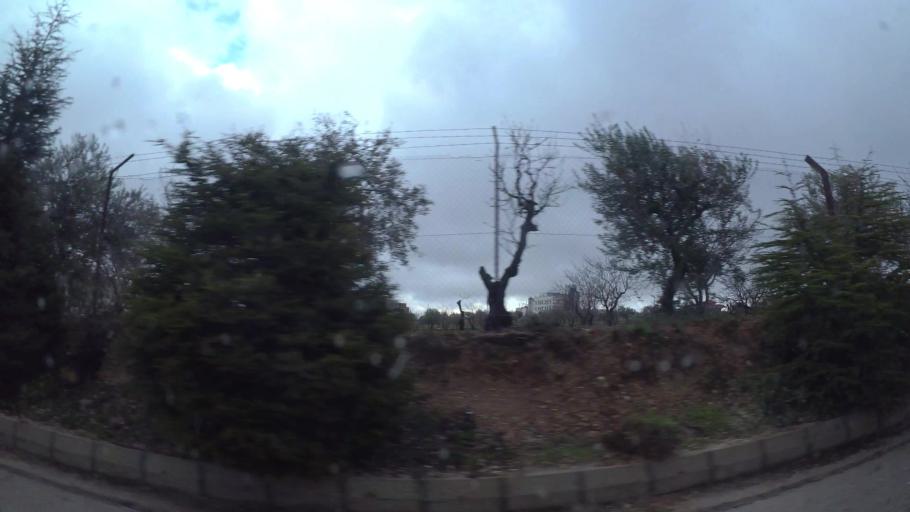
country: JO
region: Amman
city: Al Jubayhah
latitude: 32.0309
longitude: 35.8594
